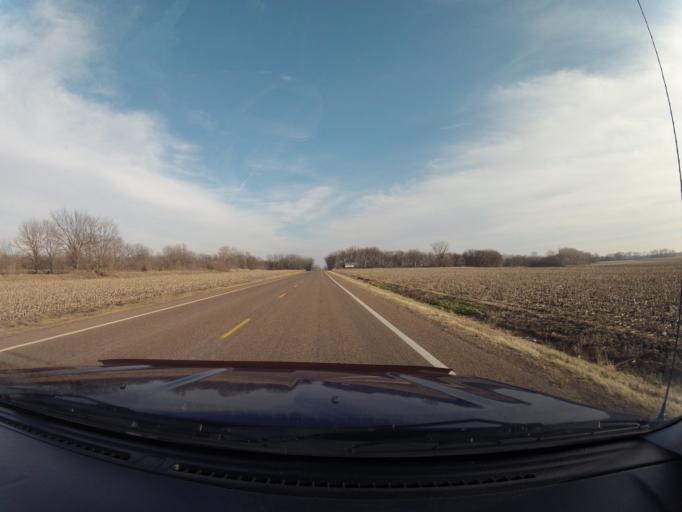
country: US
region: Kansas
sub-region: Pottawatomie County
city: Saint Marys
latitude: 39.2144
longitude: -96.1175
